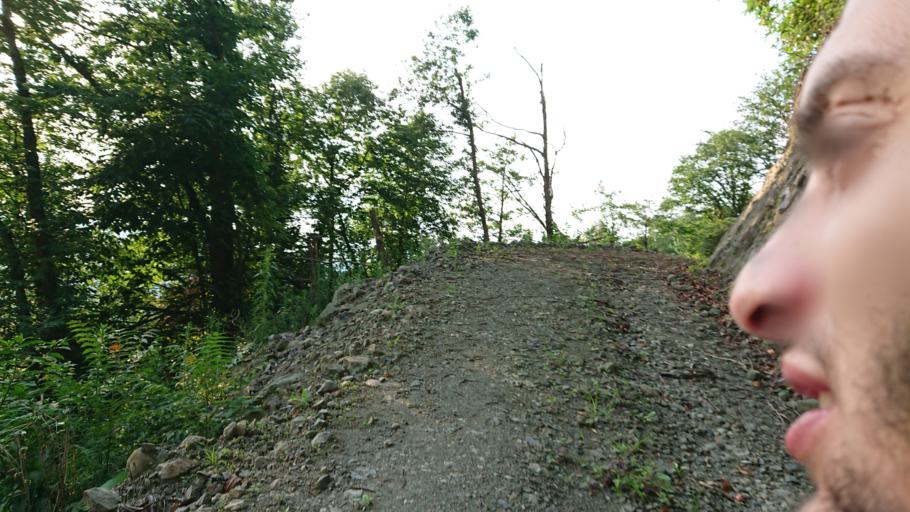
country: TR
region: Rize
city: Rize
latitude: 40.9891
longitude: 40.5050
